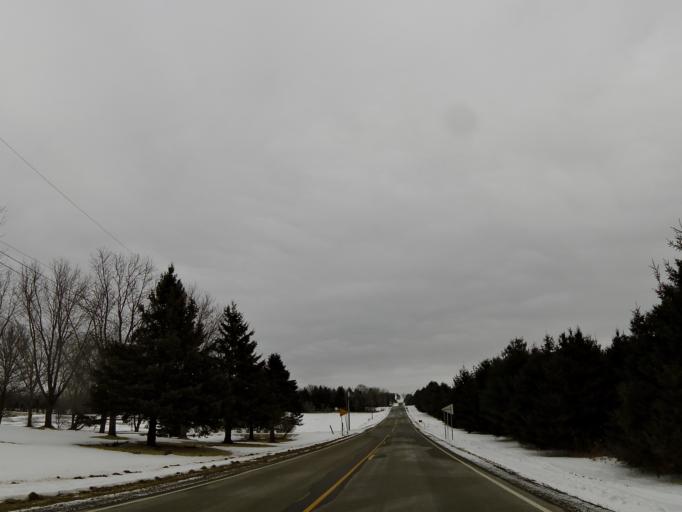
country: US
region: Wisconsin
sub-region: Pierce County
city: Prescott
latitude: 44.8189
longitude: -92.8255
